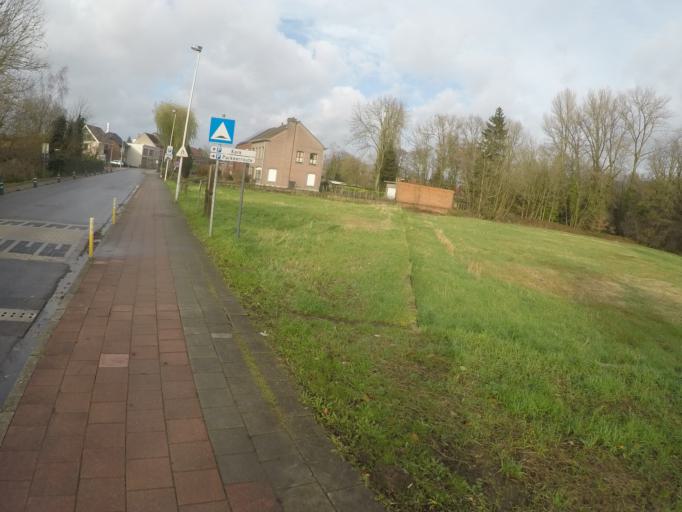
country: BE
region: Flanders
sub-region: Provincie Antwerpen
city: Wijnegem
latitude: 51.2233
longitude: 4.5231
